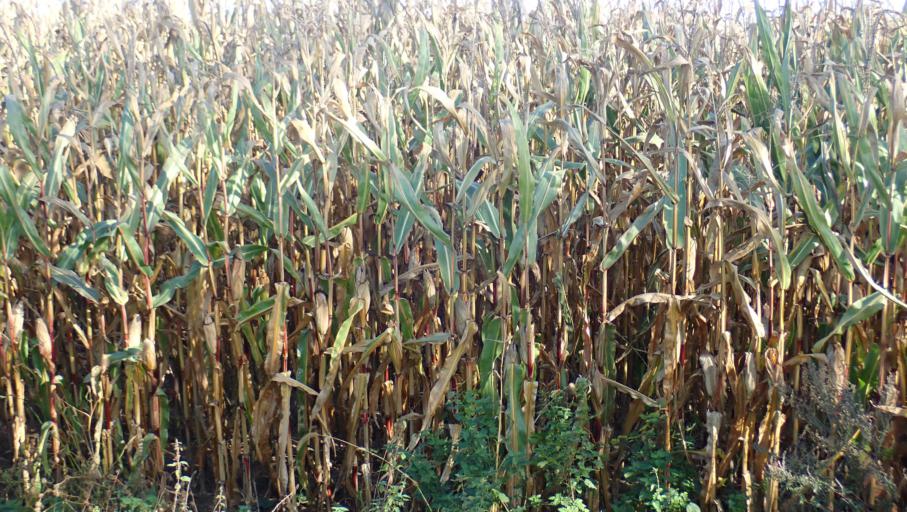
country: BE
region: Flanders
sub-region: Provincie Oost-Vlaanderen
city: Stekene
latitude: 51.1665
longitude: 4.0116
